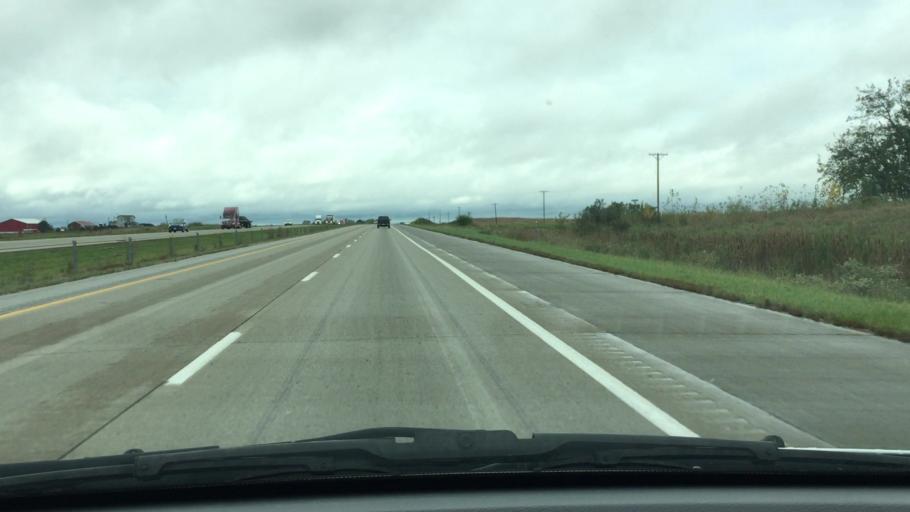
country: US
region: Iowa
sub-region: Polk County
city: Bondurant
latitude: 41.6756
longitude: -93.4251
